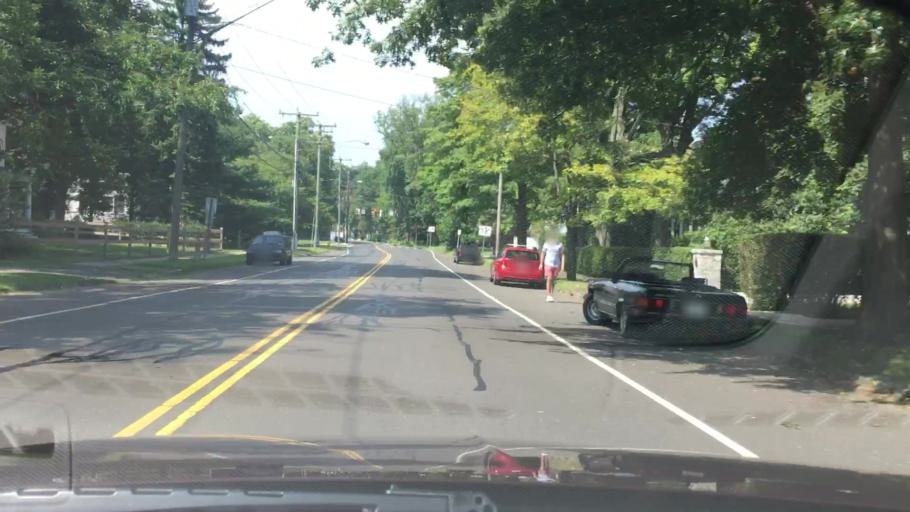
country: US
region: Connecticut
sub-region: Fairfield County
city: Norwalk
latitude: 41.1244
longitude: -73.4099
